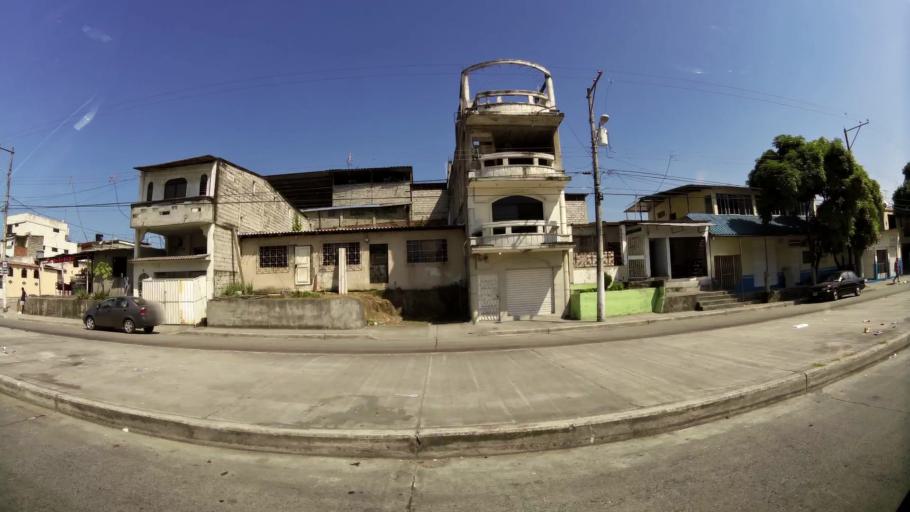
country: EC
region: Guayas
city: Eloy Alfaro
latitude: -2.1288
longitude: -79.9121
